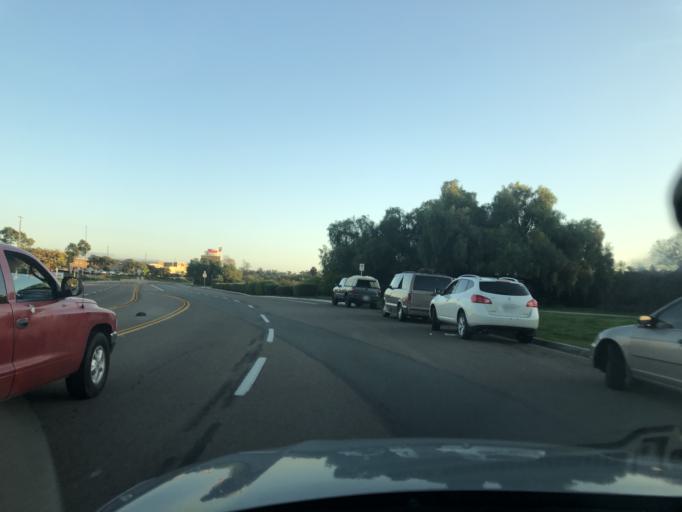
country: US
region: California
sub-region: San Diego County
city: Chula Vista
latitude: 32.6575
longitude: -117.0695
